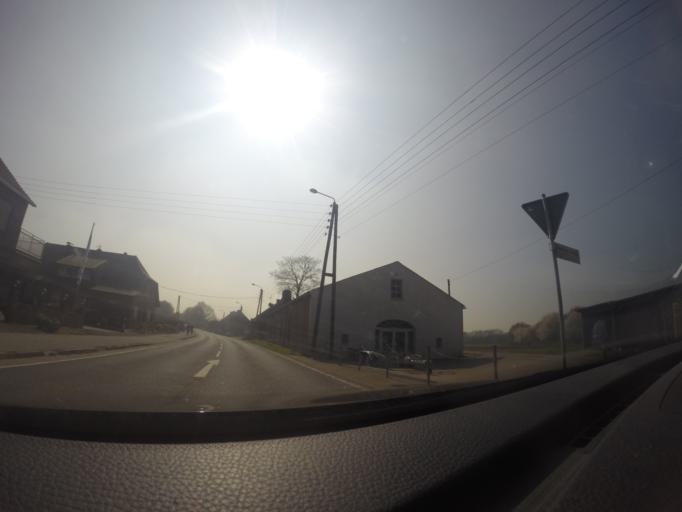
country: DE
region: North Rhine-Westphalia
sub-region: Regierungsbezirk Munster
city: Isselburg
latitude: 51.8248
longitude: 6.4180
